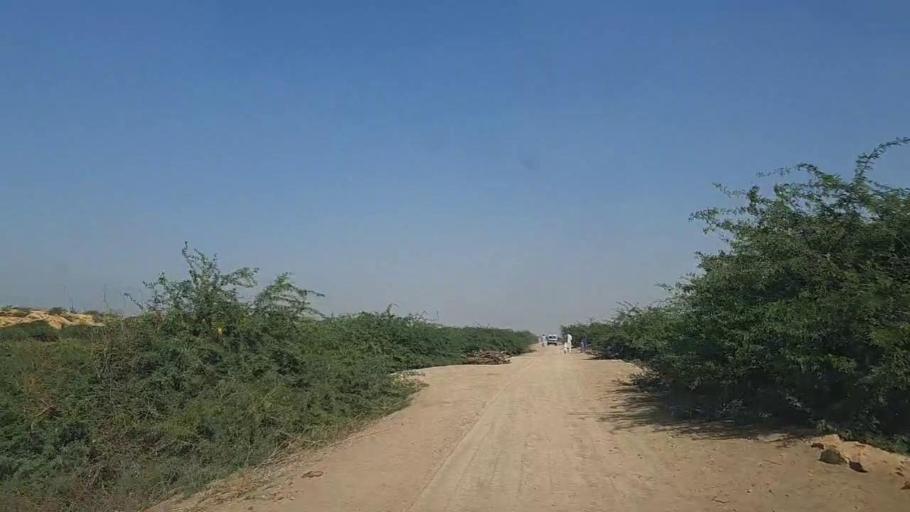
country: PK
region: Sindh
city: Daro Mehar
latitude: 24.8716
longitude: 68.0482
